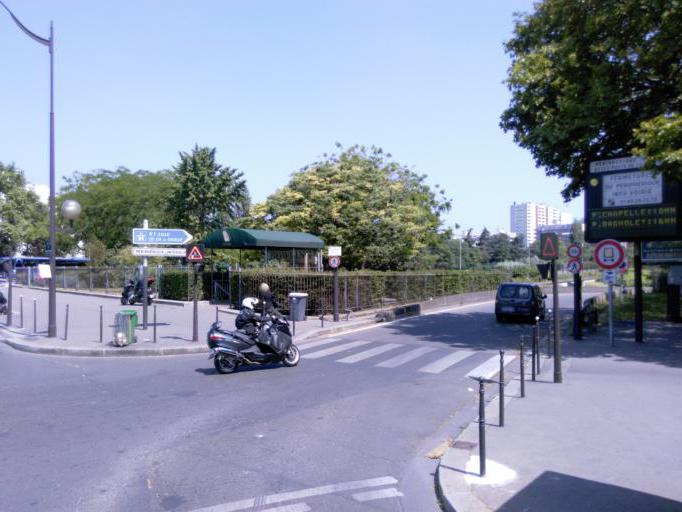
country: FR
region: Ile-de-France
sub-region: Departement des Hauts-de-Seine
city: Levallois-Perret
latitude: 48.8865
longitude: 2.2902
